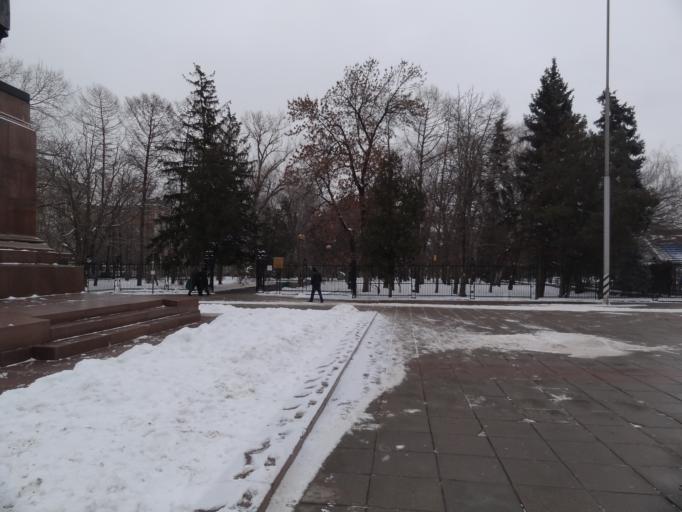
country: RU
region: Saratov
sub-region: Saratovskiy Rayon
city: Saratov
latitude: 51.5297
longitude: 46.0351
